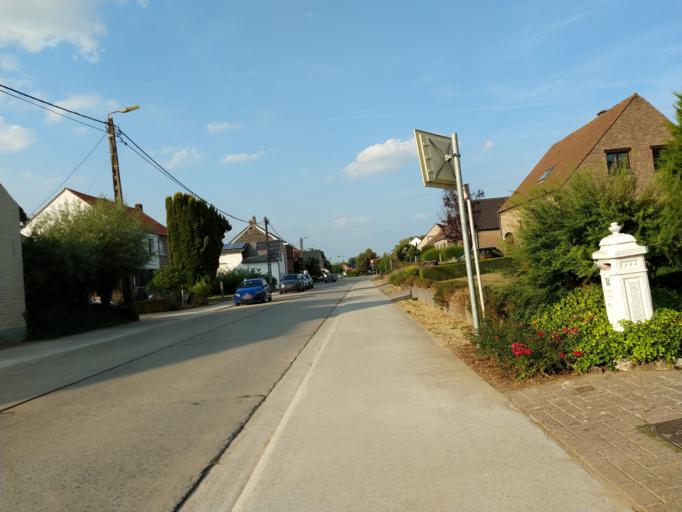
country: BE
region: Flanders
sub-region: Provincie Vlaams-Brabant
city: Bierbeek
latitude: 50.8335
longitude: 4.7912
